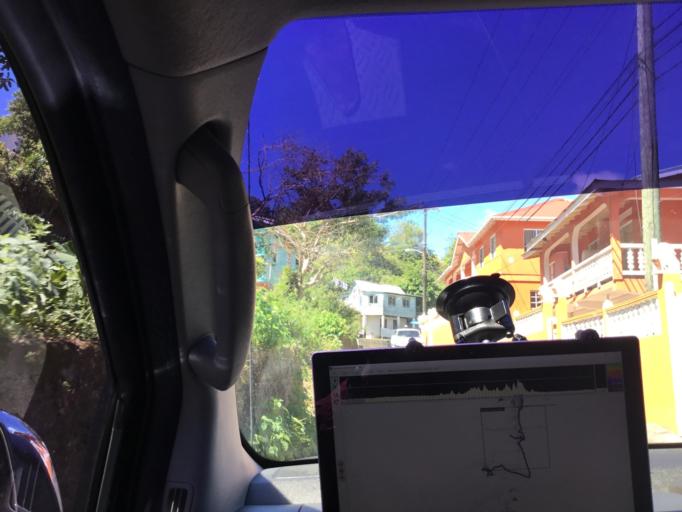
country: VC
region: Charlotte
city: Byera Village
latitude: 13.2455
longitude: -61.1412
